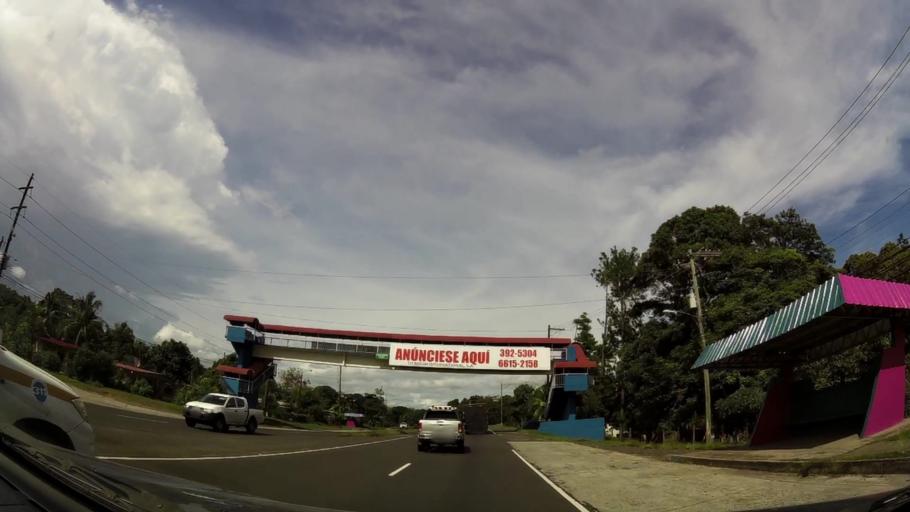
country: PA
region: Panama
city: Capira
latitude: 8.7379
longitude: -79.8821
